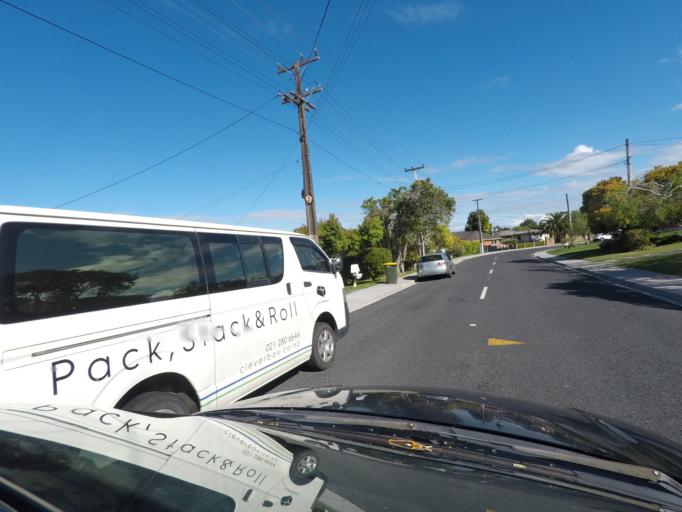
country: NZ
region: Auckland
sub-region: Auckland
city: Rosebank
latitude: -36.8635
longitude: 174.6523
